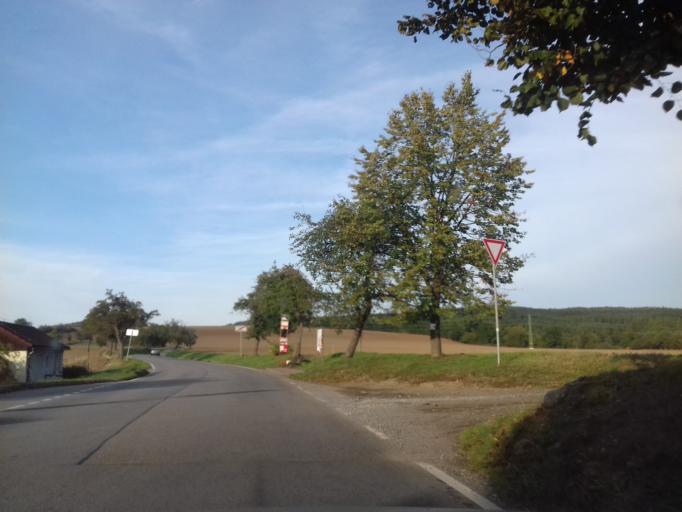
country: CZ
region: Central Bohemia
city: Kamenny Privoz
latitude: 49.8667
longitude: 14.5036
